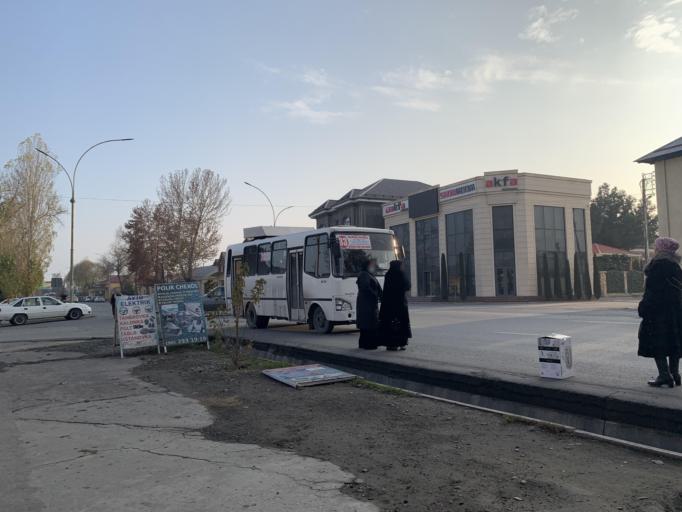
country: UZ
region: Fergana
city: Qo`qon
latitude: 40.5395
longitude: 70.9240
